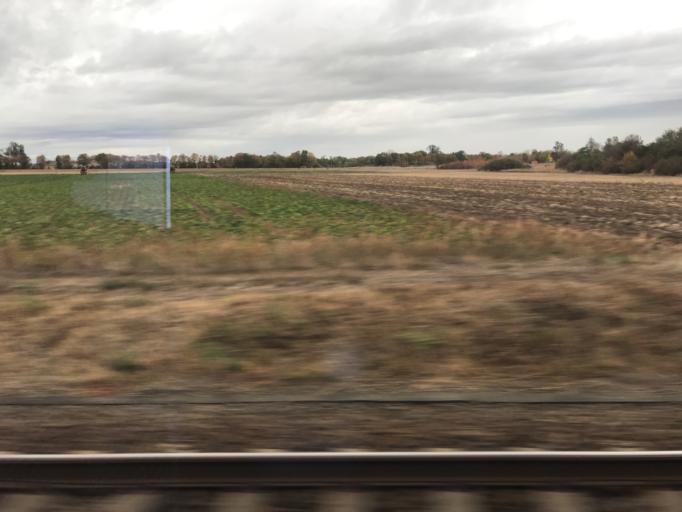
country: DE
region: Hesse
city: Gernsheim
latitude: 49.7408
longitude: 8.4938
